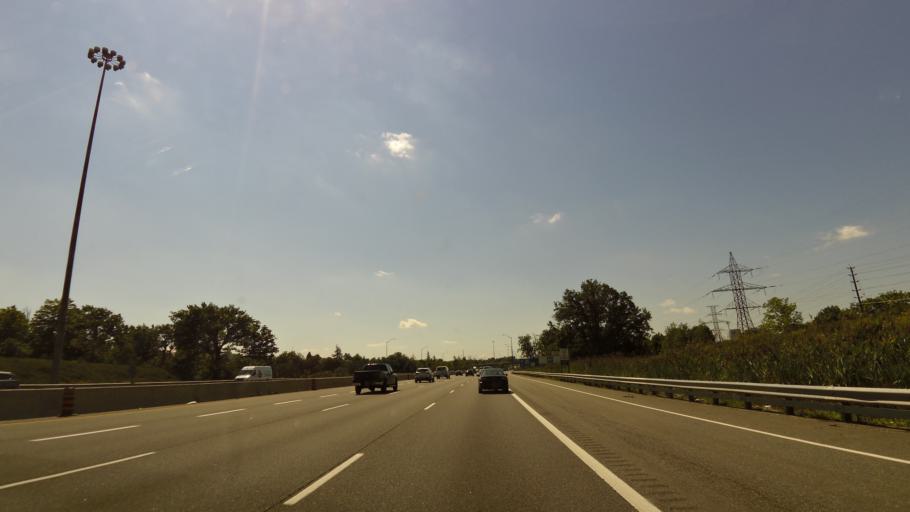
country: CA
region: Ontario
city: Mississauga
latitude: 43.5643
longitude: -79.6815
